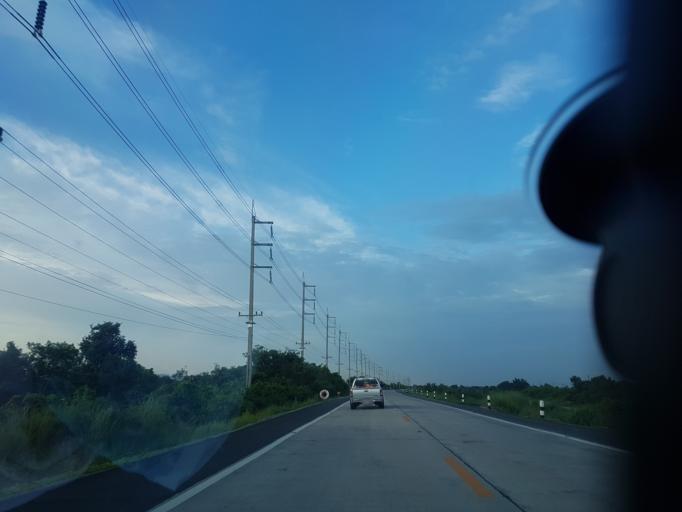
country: TH
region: Phra Nakhon Si Ayutthaya
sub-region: Amphoe Tha Ruea
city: Tha Ruea
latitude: 14.5359
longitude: 100.7496
